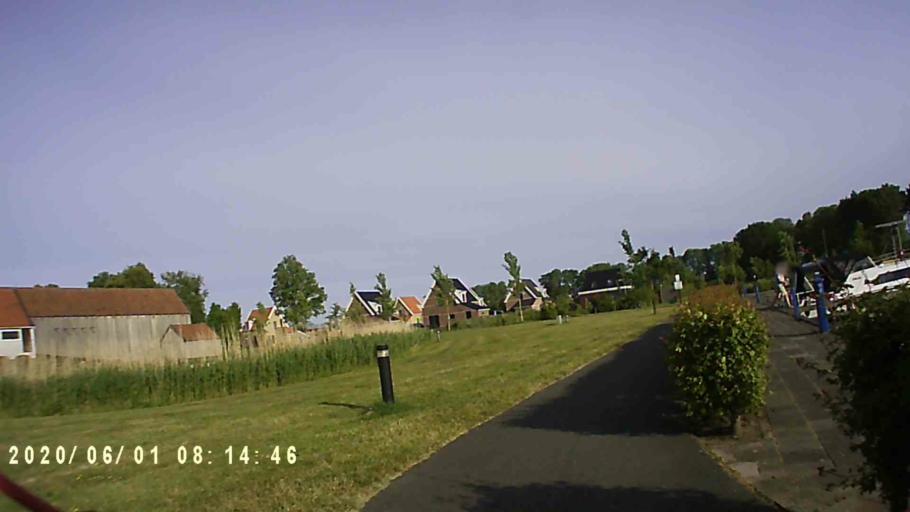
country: NL
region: Friesland
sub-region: Gemeente Ferwerderadiel
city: Burdaard
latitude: 53.2963
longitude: 5.8818
